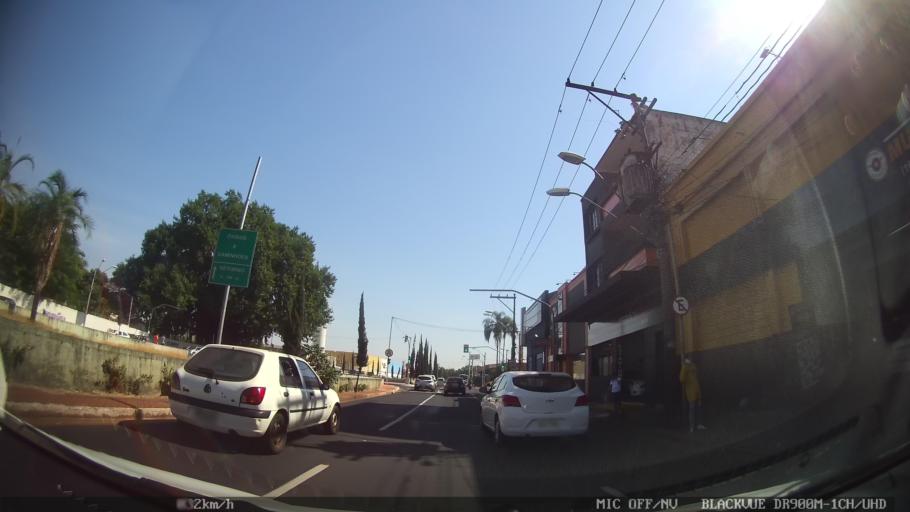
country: BR
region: Sao Paulo
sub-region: Ribeirao Preto
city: Ribeirao Preto
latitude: -21.1688
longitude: -47.8114
